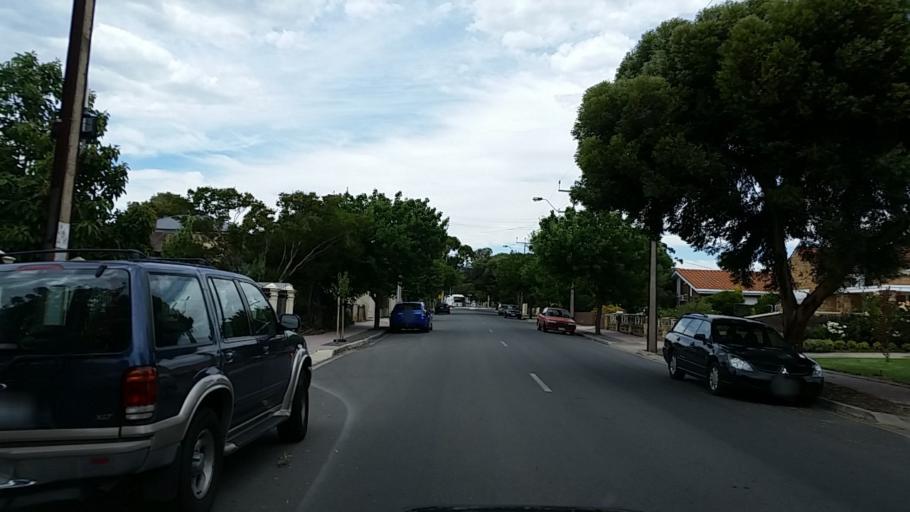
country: AU
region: South Australia
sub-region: Norwood Payneham St Peters
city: Trinity Gardens
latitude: -34.9061
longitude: 138.6438
